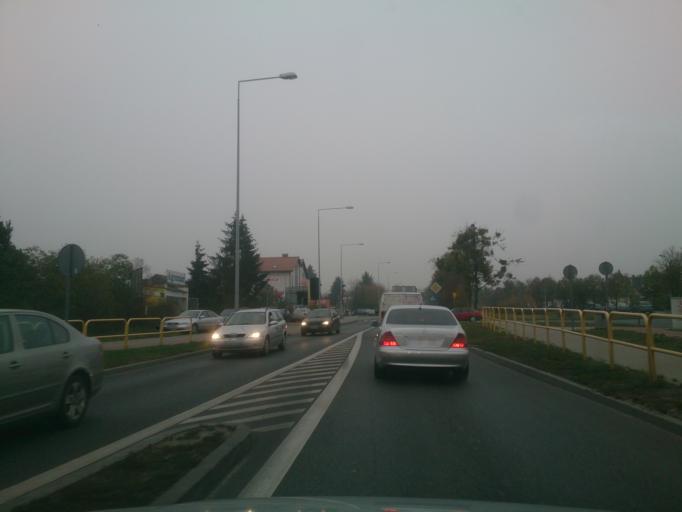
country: PL
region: Kujawsko-Pomorskie
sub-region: Powiat brodnicki
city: Brodnica
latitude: 53.2604
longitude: 19.3857
